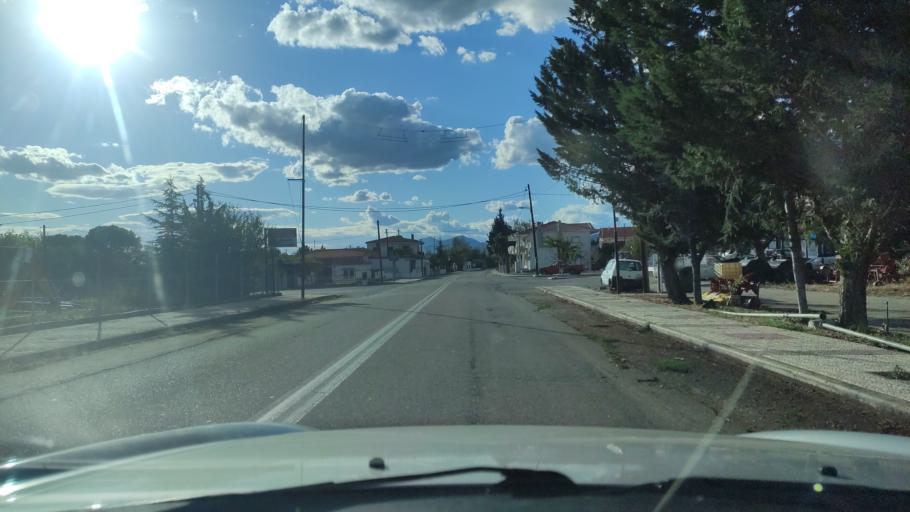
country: GR
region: East Macedonia and Thrace
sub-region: Nomos Xanthis
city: Selero
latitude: 41.1223
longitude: 25.0661
